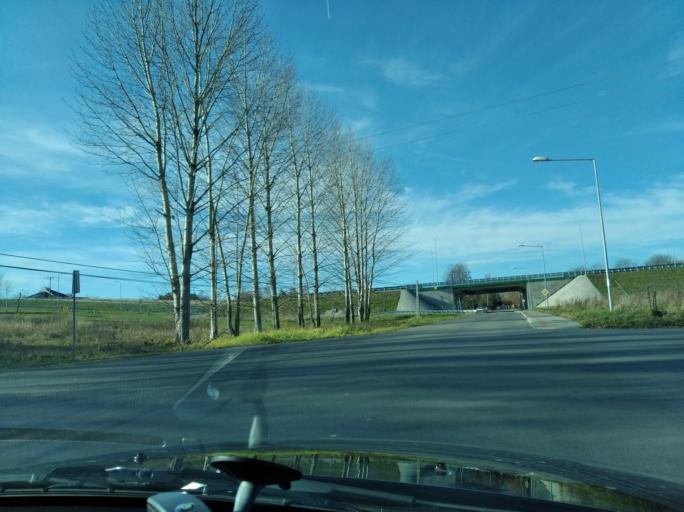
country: PL
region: Subcarpathian Voivodeship
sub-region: Powiat rzeszowski
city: Kielanowka
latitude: 50.0108
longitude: 21.9232
